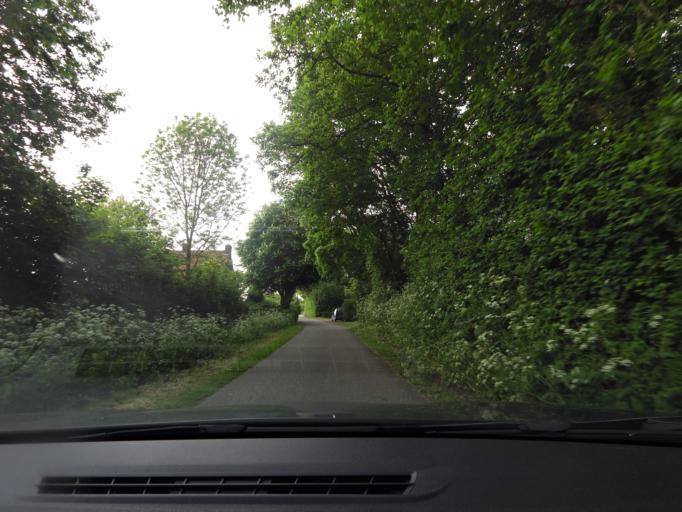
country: NL
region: Zeeland
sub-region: Schouwen-Duiveland
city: Scharendijke
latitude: 51.8019
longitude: 3.8640
